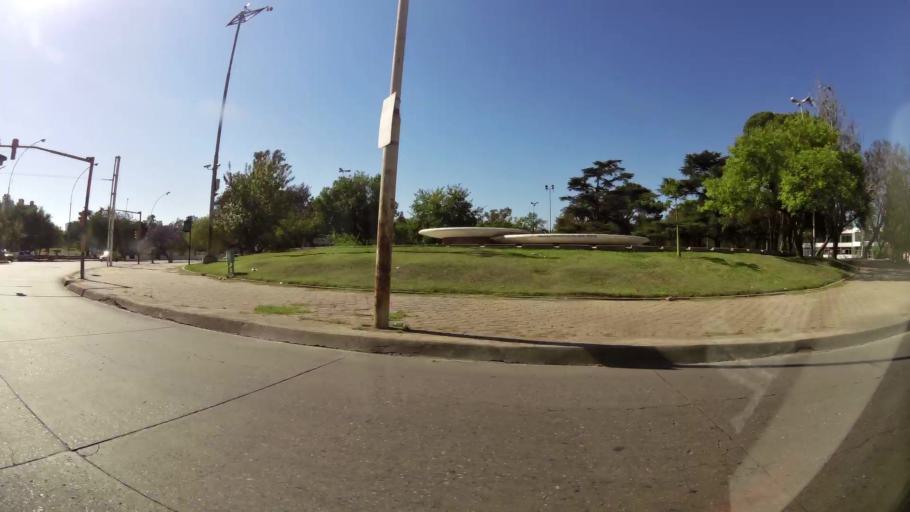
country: AR
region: Cordoba
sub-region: Departamento de Capital
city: Cordoba
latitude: -31.4325
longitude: -64.1944
